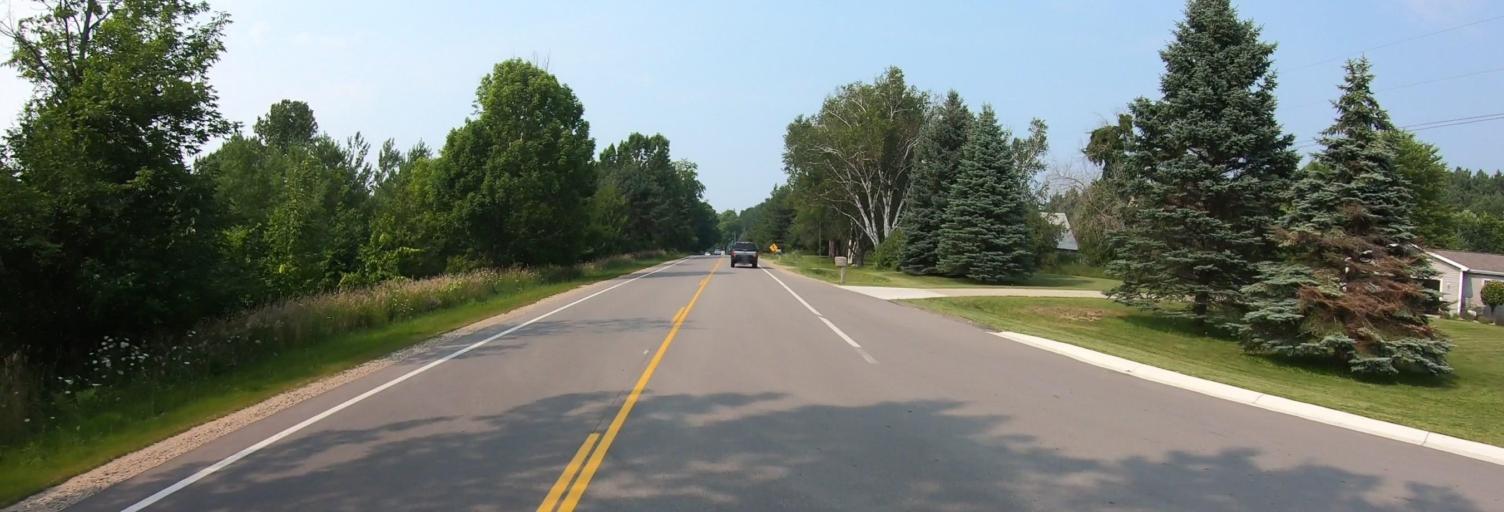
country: US
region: Michigan
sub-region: Charlevoix County
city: Charlevoix
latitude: 45.2519
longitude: -85.2612
